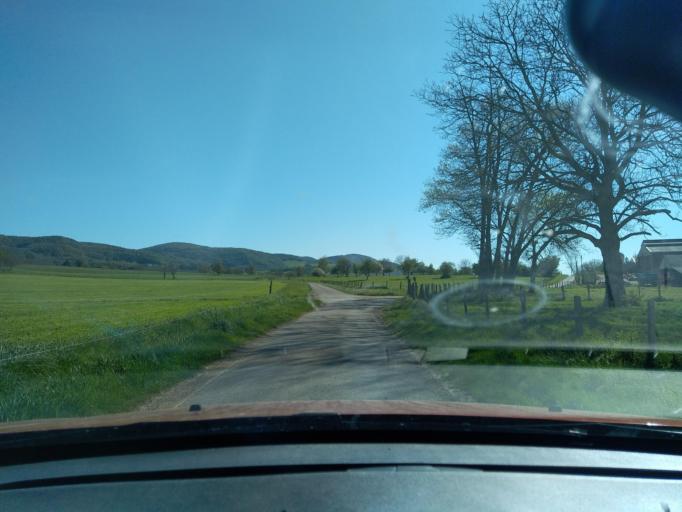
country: FR
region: Franche-Comte
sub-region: Departement du Jura
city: Montmorot
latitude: 46.6108
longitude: 5.4807
